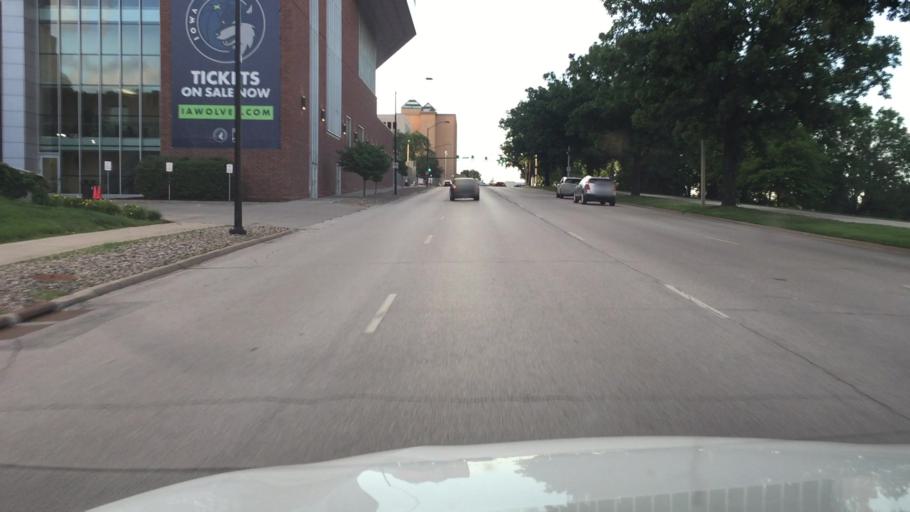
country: US
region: Iowa
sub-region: Polk County
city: Des Moines
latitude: 41.5917
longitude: -93.6204
